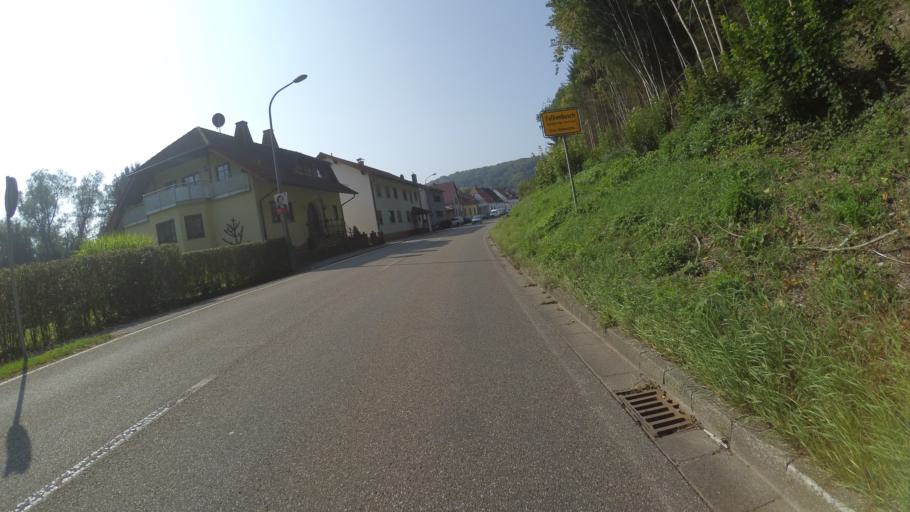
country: DE
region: Rheinland-Pfalz
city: Dellfeld
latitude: 49.2306
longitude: 7.4692
